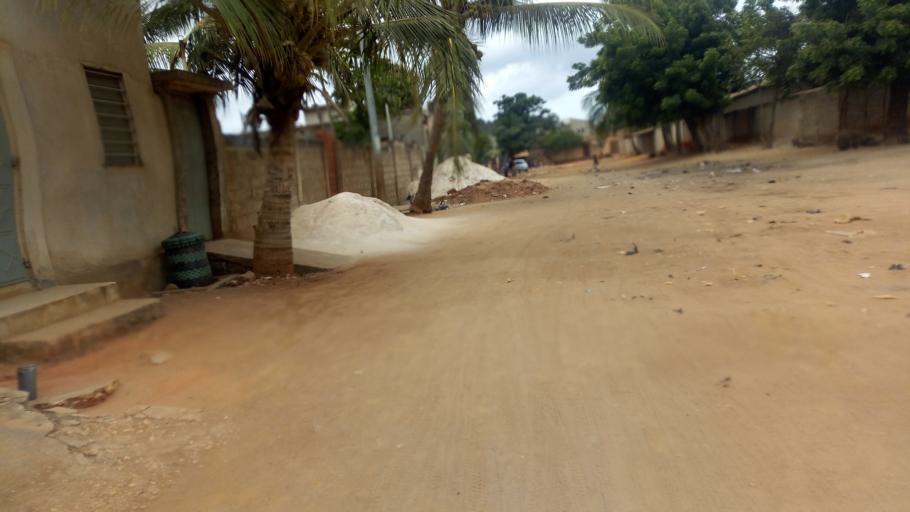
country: TG
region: Maritime
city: Lome
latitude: 6.2298
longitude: 1.1861
